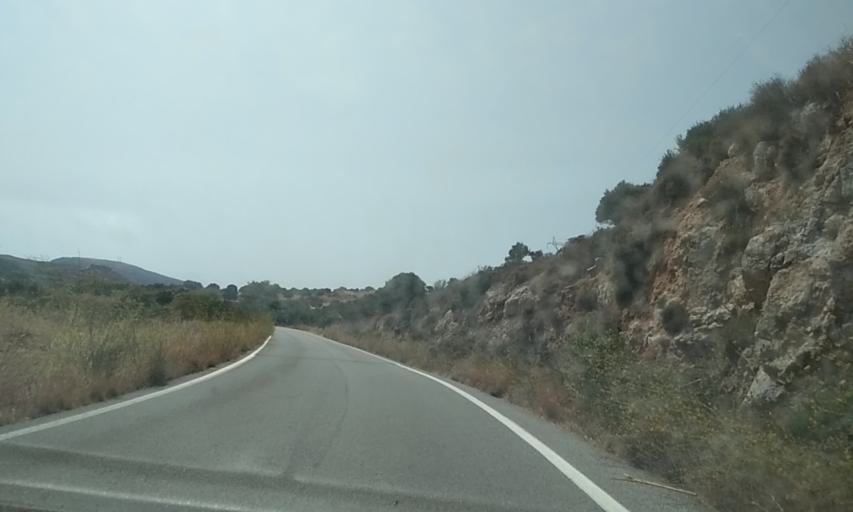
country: GR
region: Crete
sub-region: Nomos Lasithiou
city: Siteia
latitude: 35.1206
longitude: 26.0619
